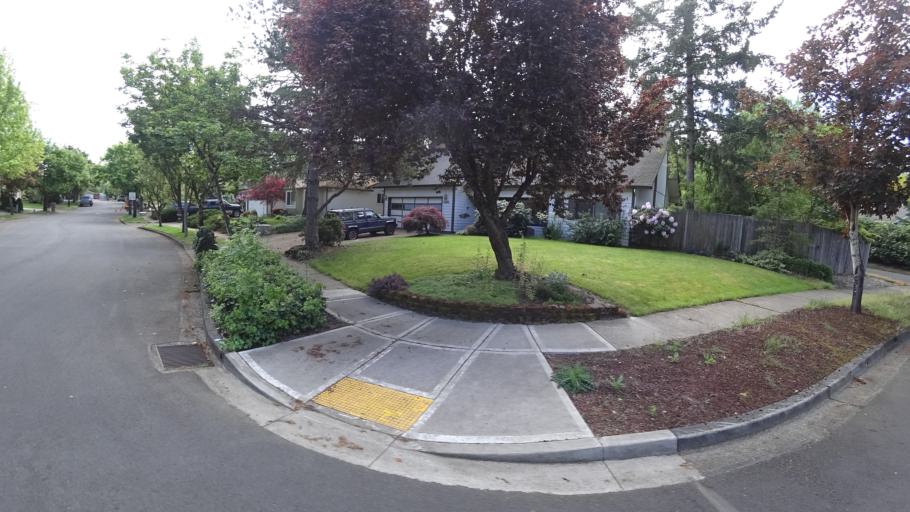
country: US
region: Oregon
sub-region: Washington County
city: Beaverton
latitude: 45.4689
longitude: -122.8075
